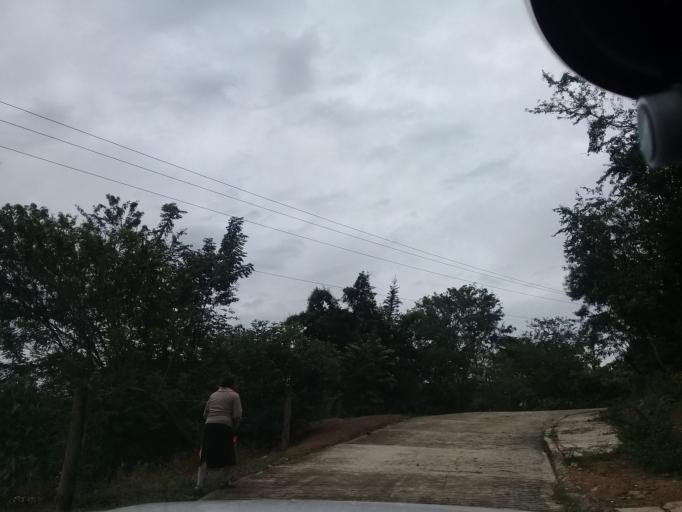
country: MX
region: Veracruz
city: Platon Sanchez
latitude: 21.2158
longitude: -98.3728
